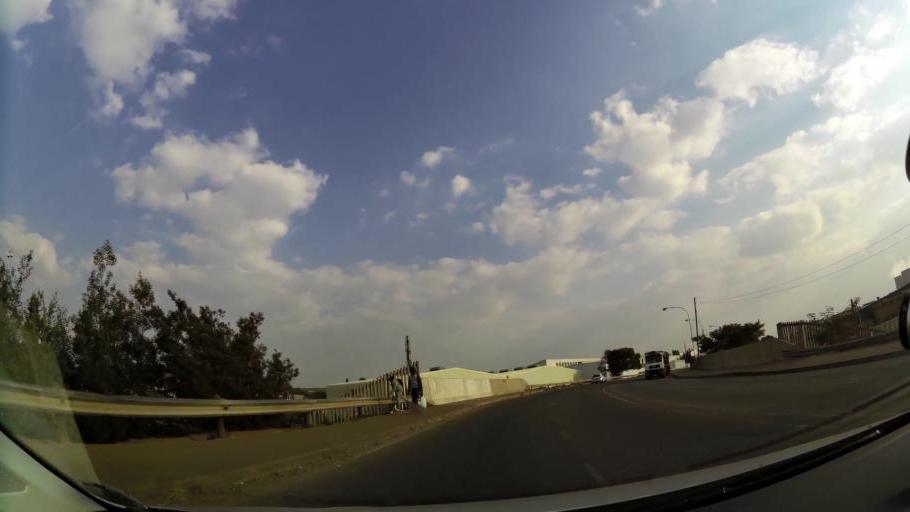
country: ZA
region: Gauteng
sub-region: City of Johannesburg Metropolitan Municipality
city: Modderfontein
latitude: -26.1186
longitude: 28.2077
